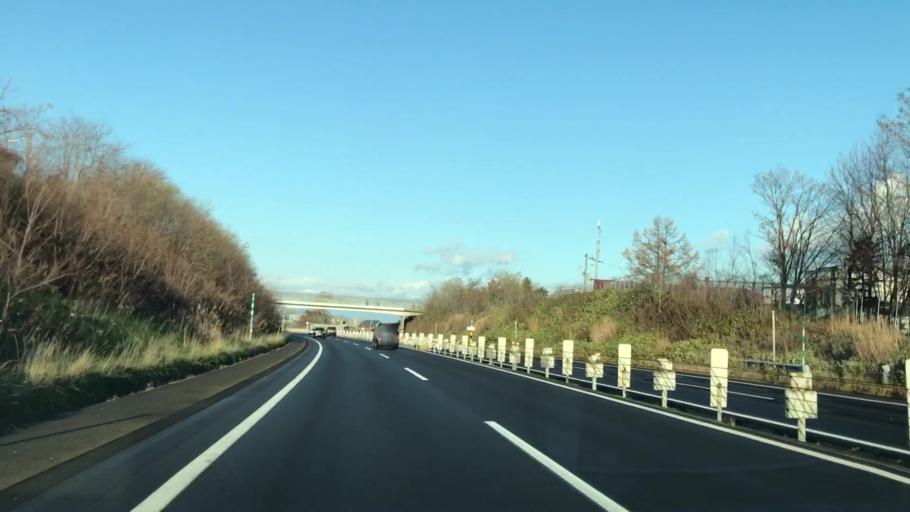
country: JP
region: Hokkaido
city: Sapporo
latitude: 43.1162
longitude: 141.2333
